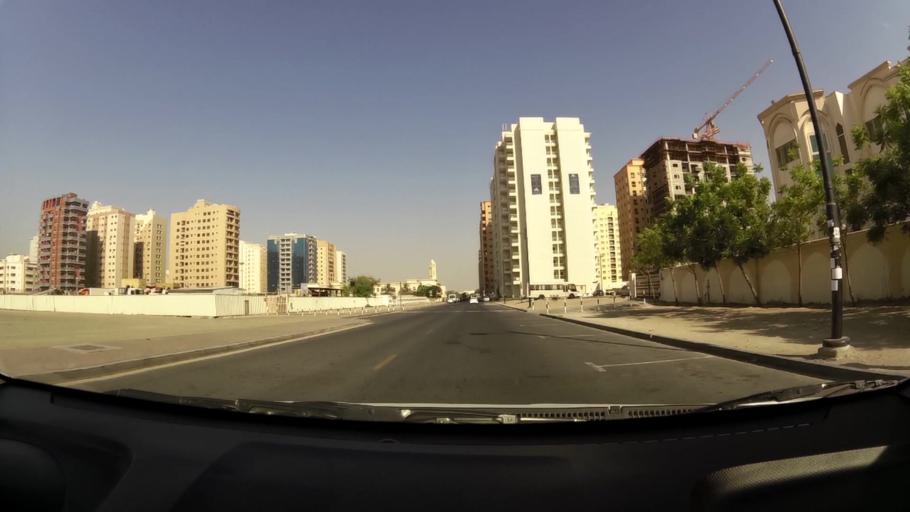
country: AE
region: Ash Shariqah
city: Sharjah
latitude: 25.2918
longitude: 55.3762
